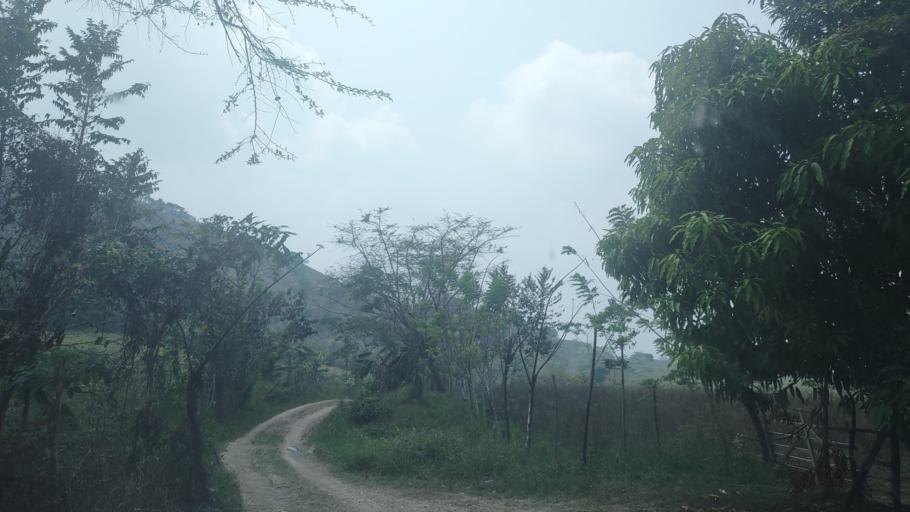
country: MX
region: Tabasco
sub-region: Huimanguillo
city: Francisco Rueda
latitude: 17.6688
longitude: -93.8859
